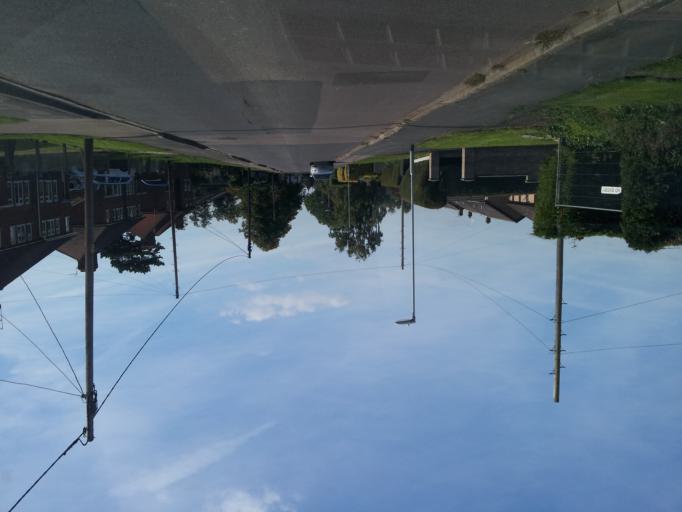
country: GB
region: England
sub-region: Cambridgeshire
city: Waterbeach
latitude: 52.2709
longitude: 0.1923
